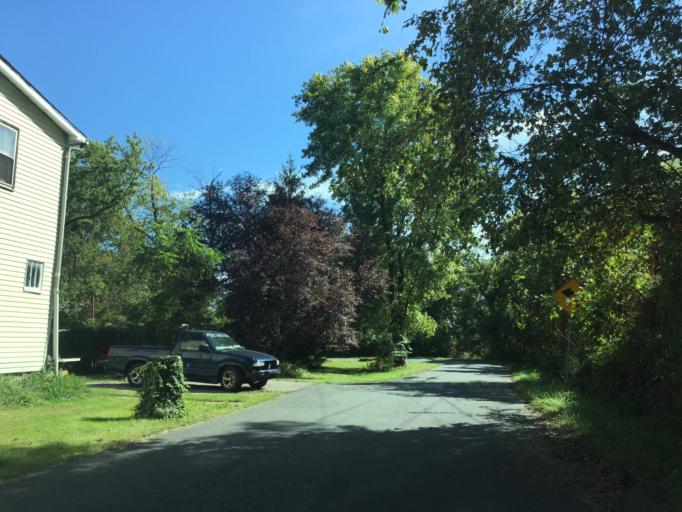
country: US
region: Maryland
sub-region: Baltimore County
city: White Marsh
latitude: 39.3823
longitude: -76.4283
